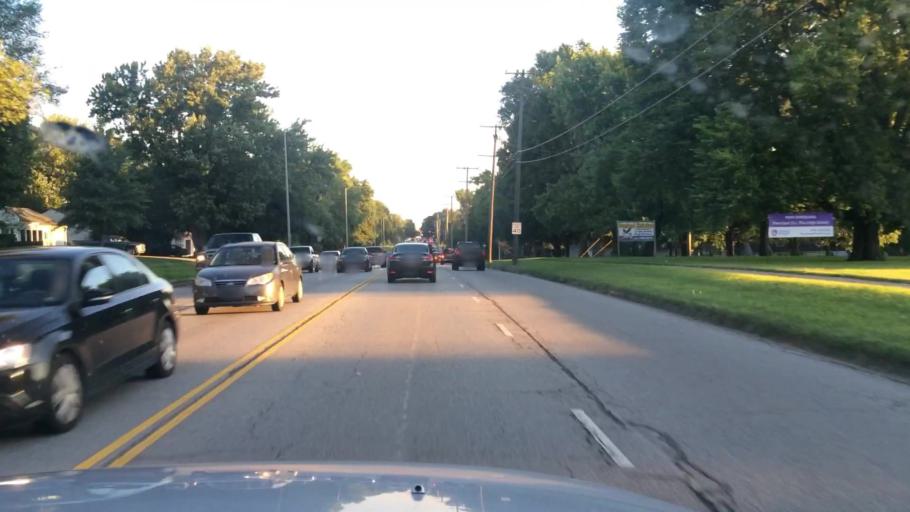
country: US
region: Kansas
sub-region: Johnson County
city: Overland Park
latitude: 38.9953
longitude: -94.6677
